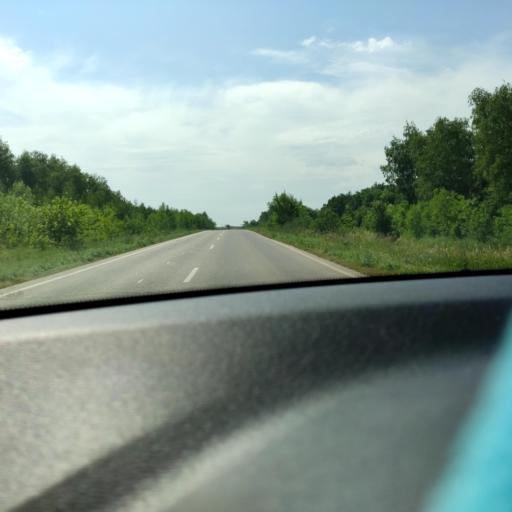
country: RU
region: Samara
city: Petra-Dubrava
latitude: 53.3432
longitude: 50.4708
